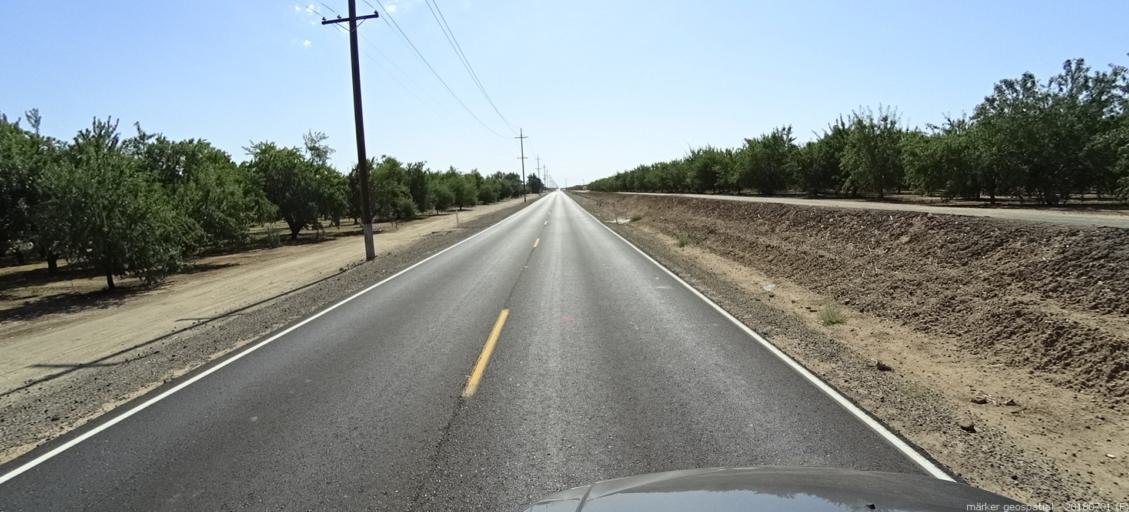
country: US
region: California
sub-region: Madera County
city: Bonadelle Ranchos-Madera Ranchos
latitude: 36.8804
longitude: -119.8883
